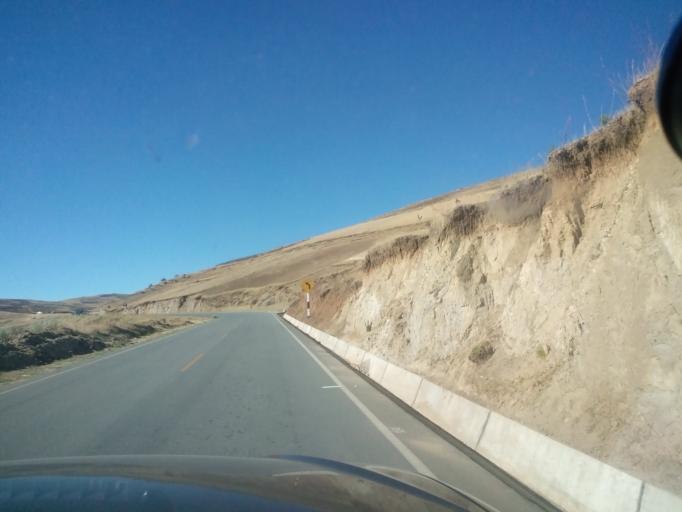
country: PE
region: Apurimac
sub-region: Provincia de Andahuaylas
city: Pacucha
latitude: -13.6621
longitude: -73.2816
